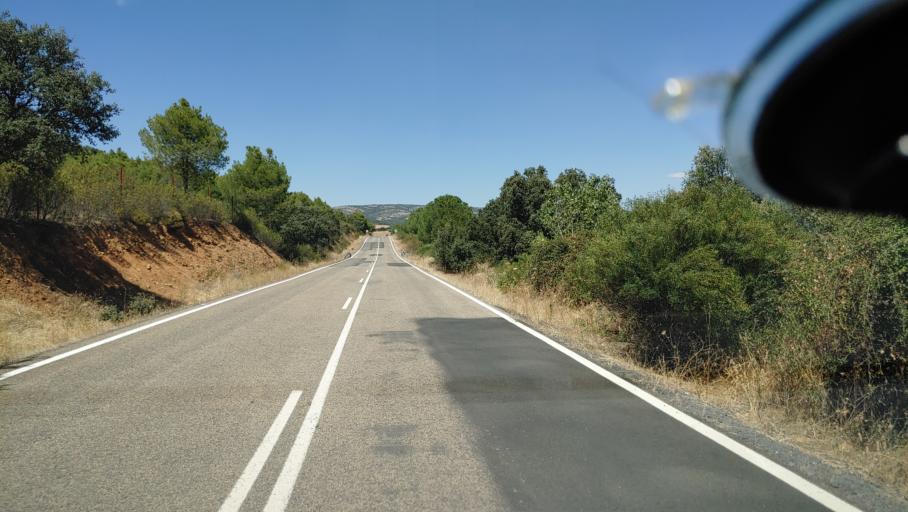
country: ES
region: Castille-La Mancha
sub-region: Provincia de Ciudad Real
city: Almaden
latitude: 38.8213
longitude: -4.7117
